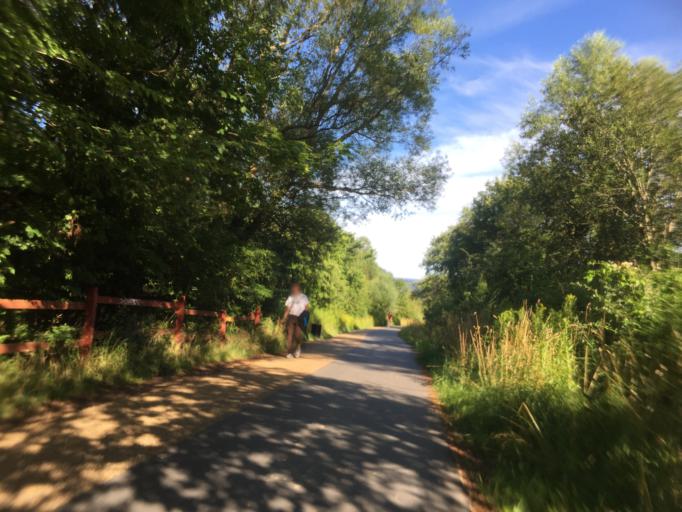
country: DK
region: Capital Region
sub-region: Kobenhavn
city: Copenhagen
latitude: 55.6597
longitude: 12.5781
